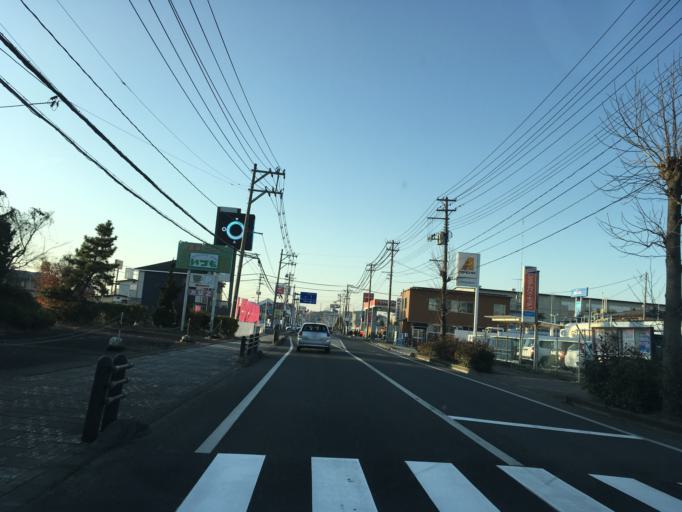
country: JP
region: Miyagi
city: Wakuya
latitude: 38.6865
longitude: 141.1889
